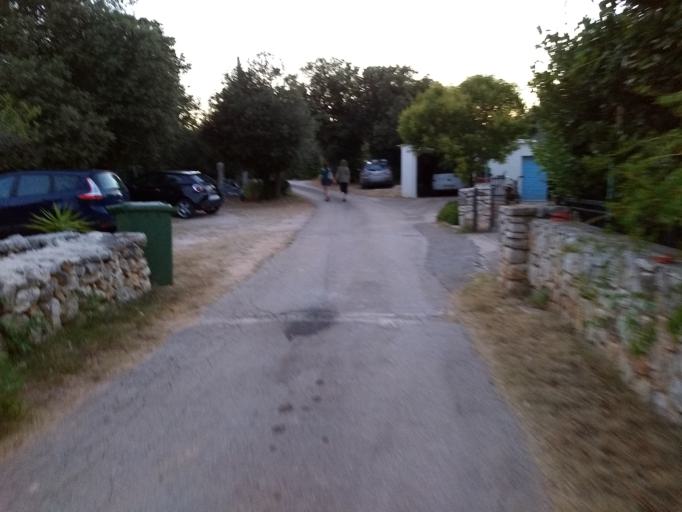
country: HR
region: Zadarska
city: Ugljan
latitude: 44.1422
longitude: 15.0837
